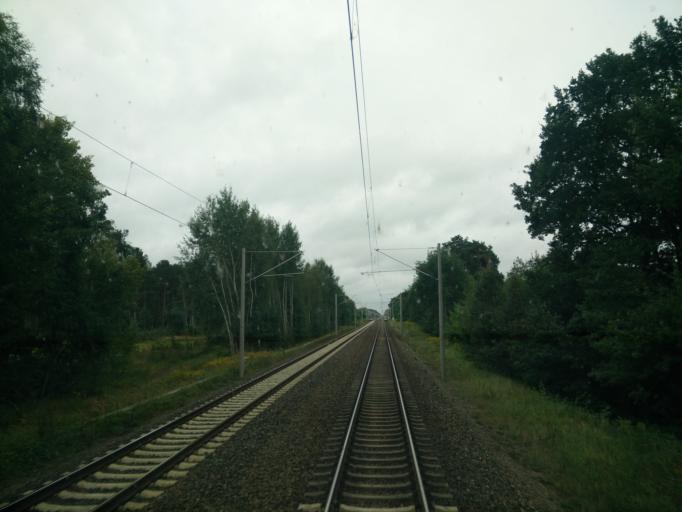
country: DE
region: Brandenburg
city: Kasel-Golzig
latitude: 51.9945
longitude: 13.7721
